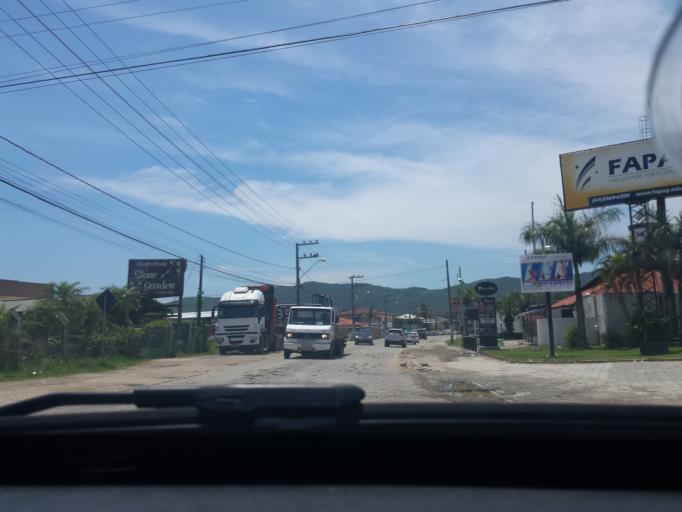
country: BR
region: Santa Catarina
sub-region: Porto Belo
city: Porto Belo
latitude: -27.1581
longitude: -48.5844
